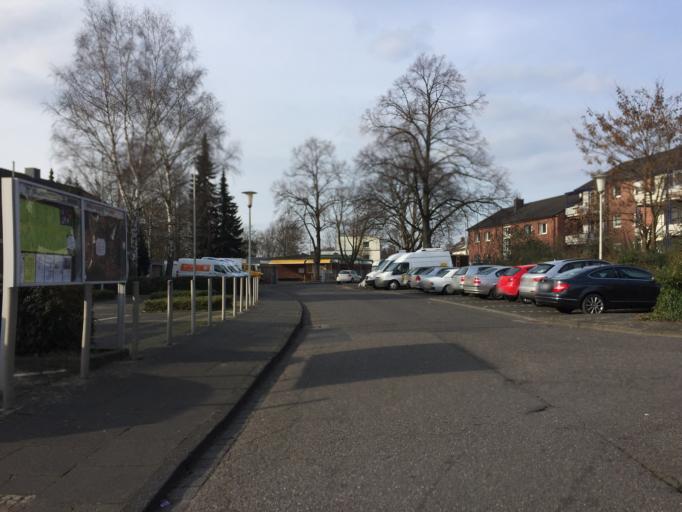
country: DE
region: North Rhine-Westphalia
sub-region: Regierungsbezirk Koln
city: Bonn
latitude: 50.7462
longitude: 7.0779
